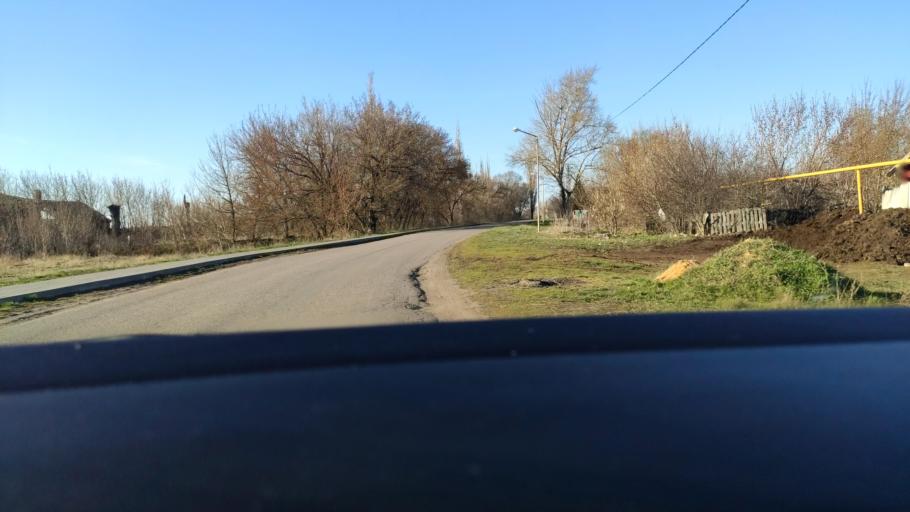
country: RU
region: Voronezj
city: Maslovka
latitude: 51.5032
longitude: 39.2935
